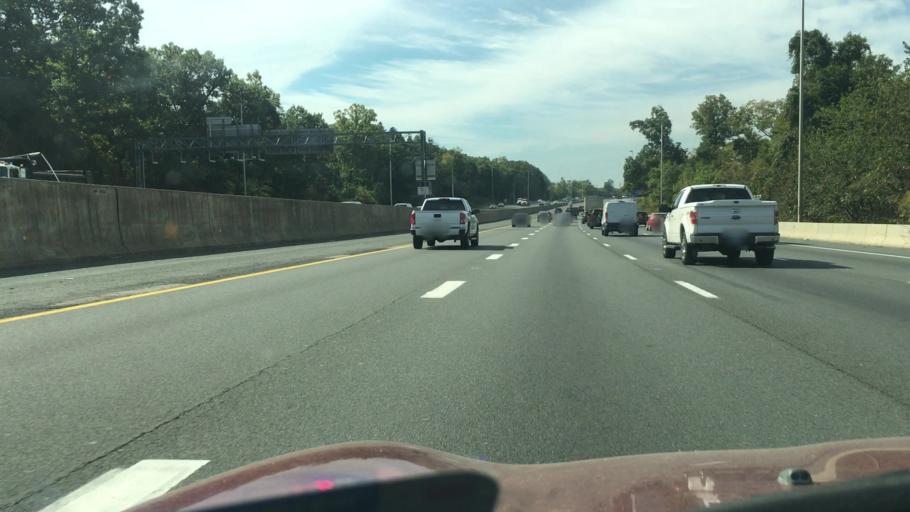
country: US
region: Virginia
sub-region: Fairfax County
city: Centreville
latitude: 38.8250
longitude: -77.4587
